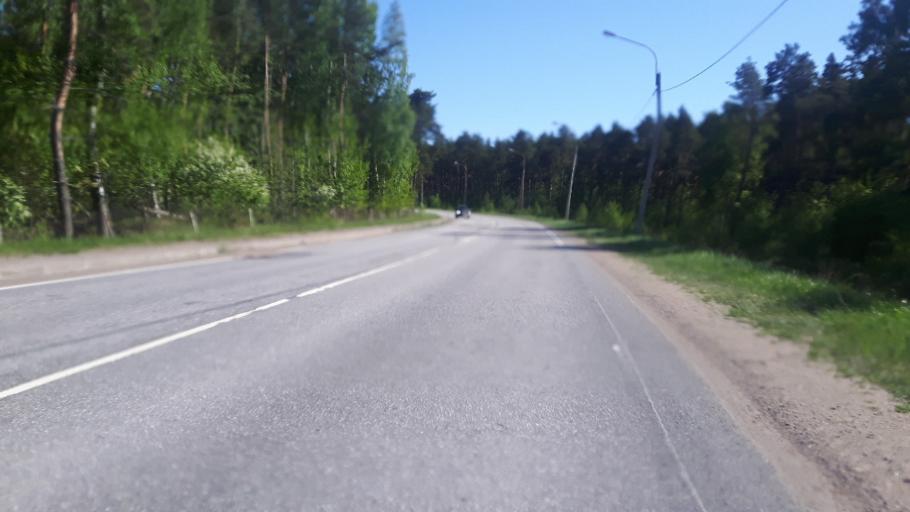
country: RU
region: Leningrad
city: Sosnovyy Bor
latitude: 60.1945
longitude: 29.0070
